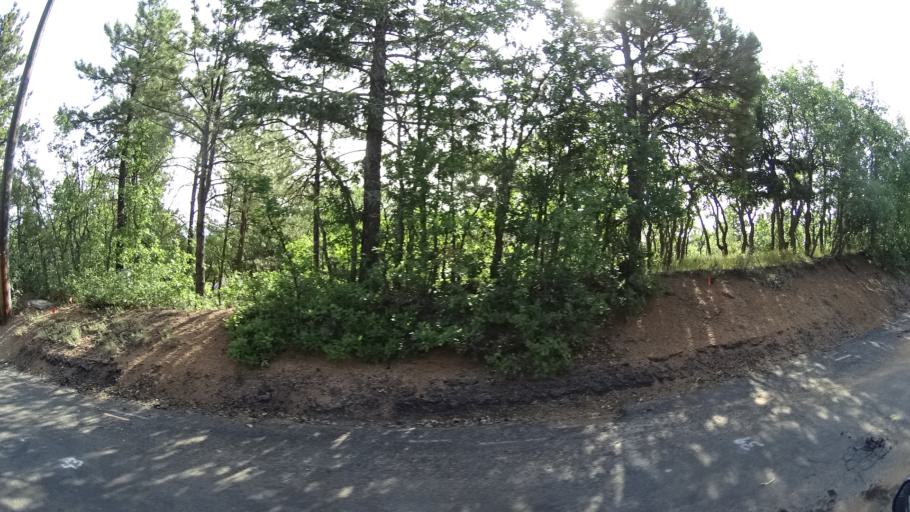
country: US
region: Colorado
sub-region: El Paso County
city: Colorado Springs
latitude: 38.8096
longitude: -104.8733
